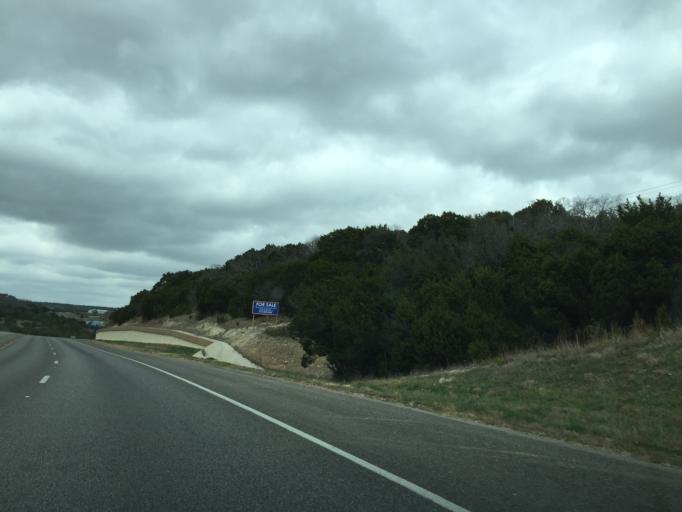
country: US
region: Texas
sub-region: Travis County
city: The Hills
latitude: 30.3351
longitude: -98.0300
